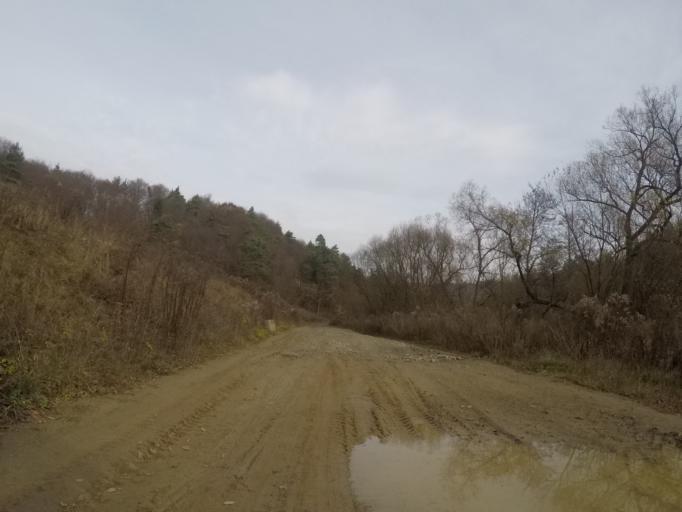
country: SK
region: Presovsky
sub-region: Okres Presov
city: Presov
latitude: 48.9459
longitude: 21.1944
